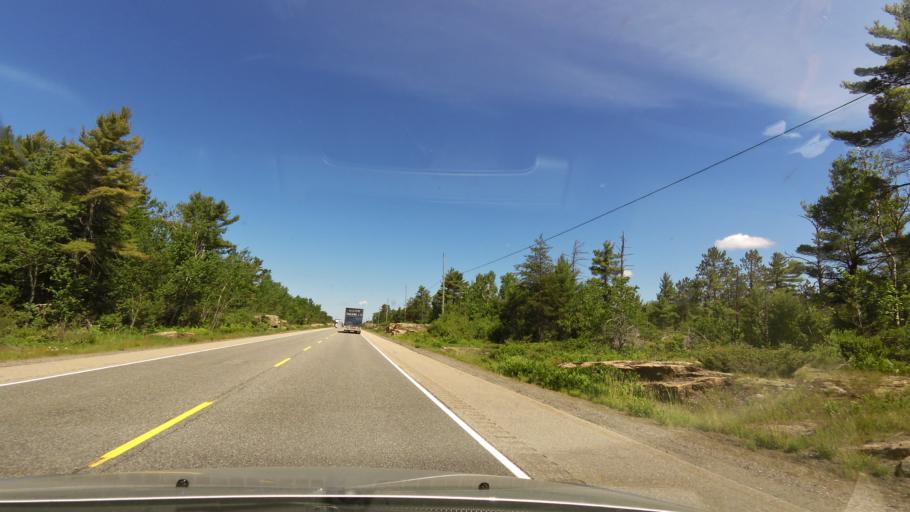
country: CA
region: Ontario
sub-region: Parry Sound District
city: Parry Sound
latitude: 45.6947
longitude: -80.4524
